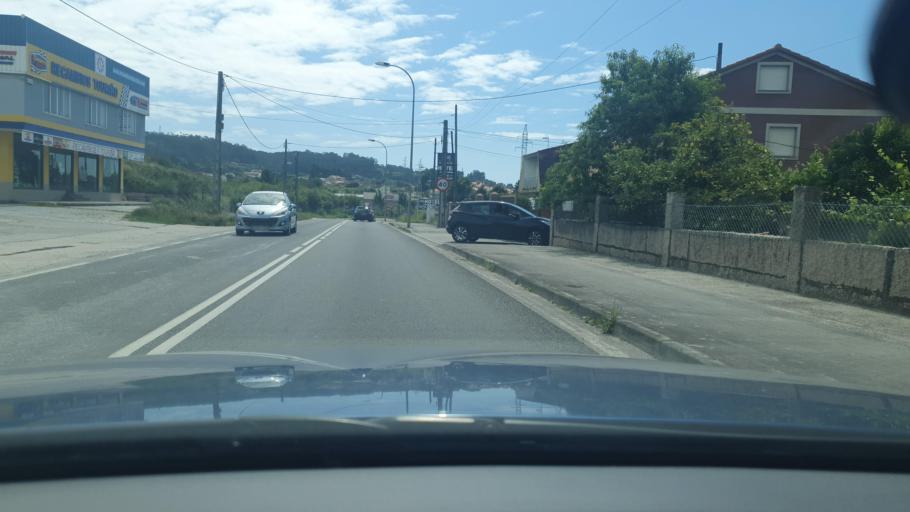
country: ES
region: Galicia
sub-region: Provincia de Pontevedra
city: Meano
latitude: 42.4458
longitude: -8.8238
